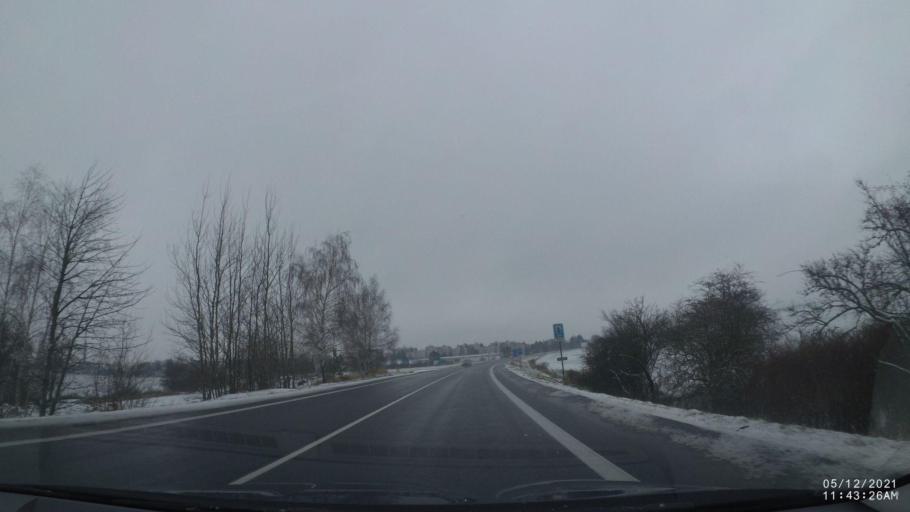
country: CZ
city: Dobruska
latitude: 50.2861
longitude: 16.1717
